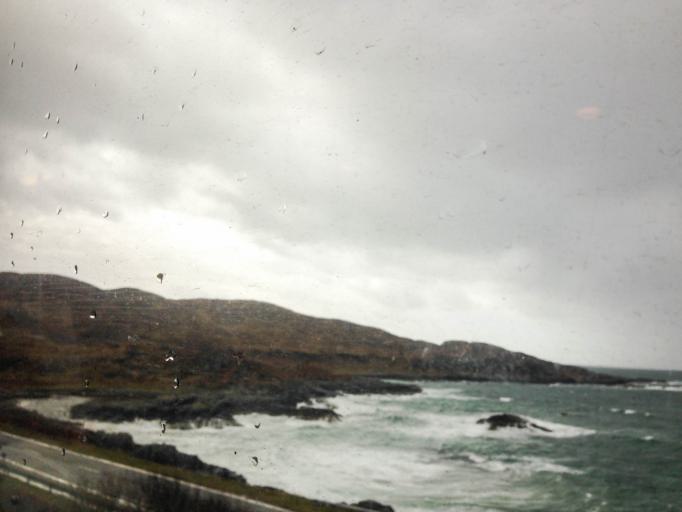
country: GB
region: Scotland
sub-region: Argyll and Bute
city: Isle Of Mull
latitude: 56.9956
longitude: -5.8312
